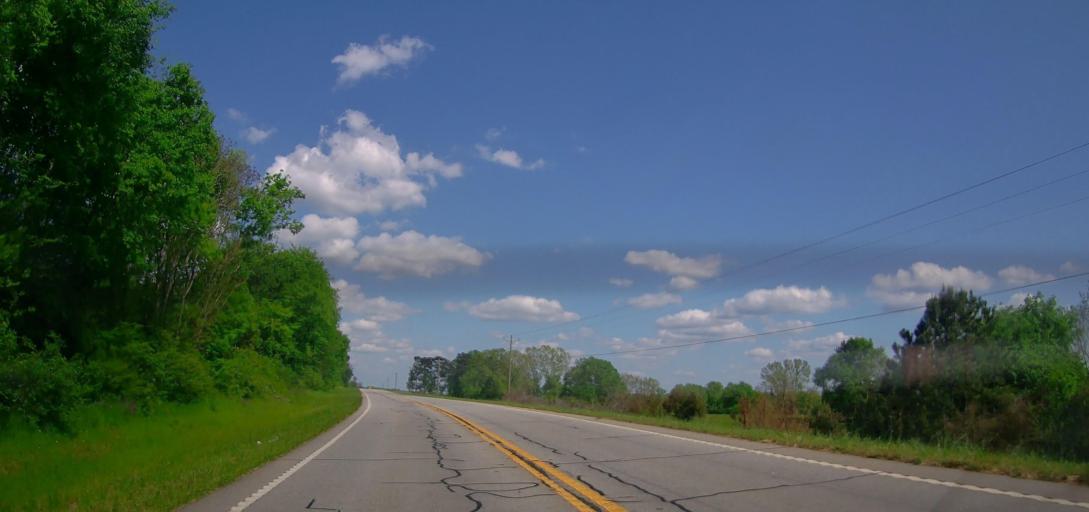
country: US
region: Georgia
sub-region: Greene County
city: Greensboro
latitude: 33.5970
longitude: -83.3001
